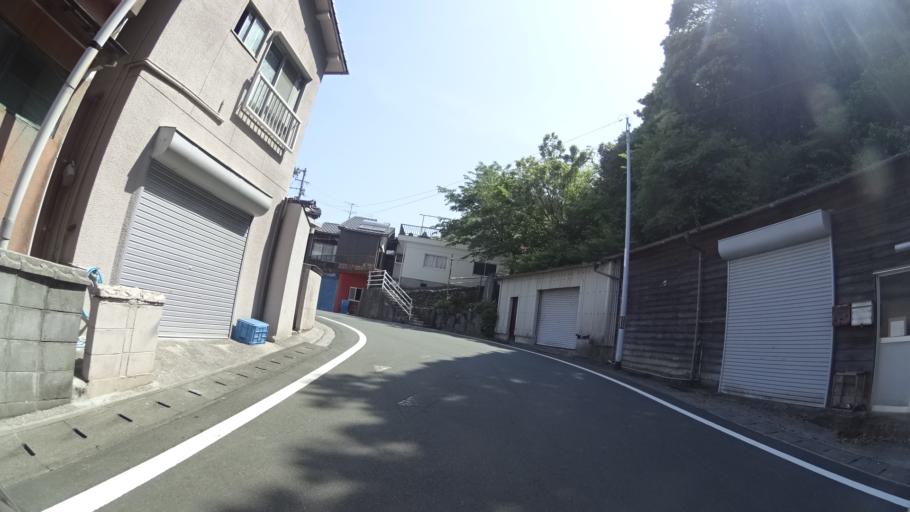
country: JP
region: Ehime
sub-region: Nishiuwa-gun
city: Ikata-cho
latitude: 33.3723
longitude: 132.0534
